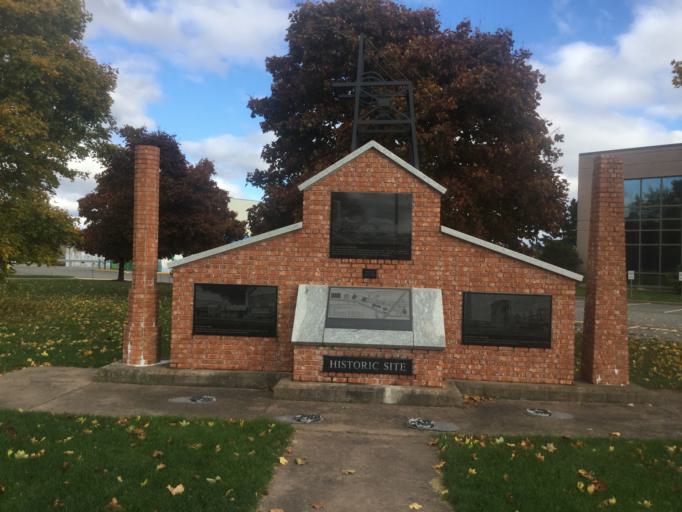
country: CA
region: Nova Scotia
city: New Glasgow
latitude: 45.5728
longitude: -62.6577
